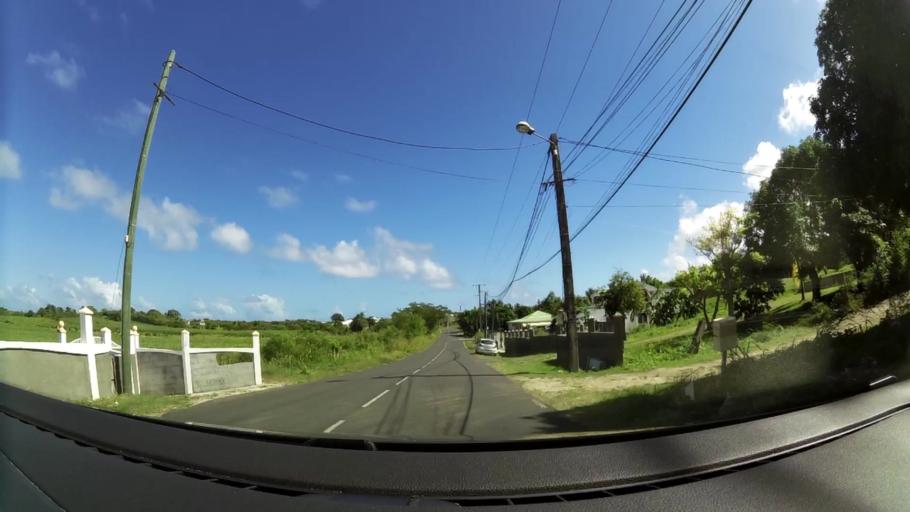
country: GP
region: Guadeloupe
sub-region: Guadeloupe
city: Petit-Canal
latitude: 16.3691
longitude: -61.4415
